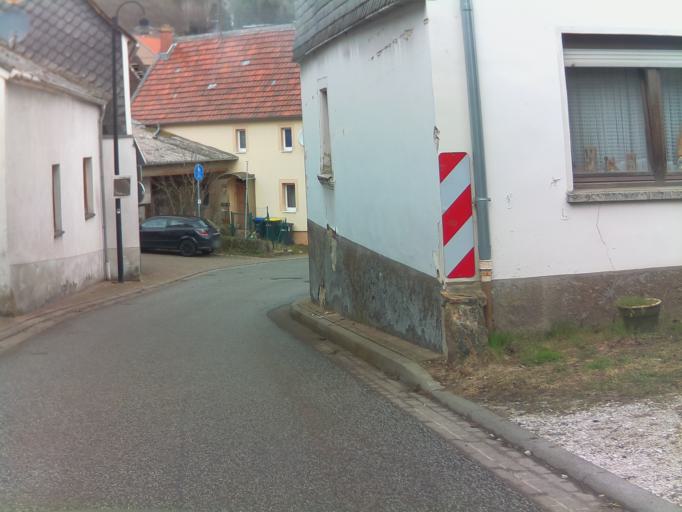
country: DE
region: Rheinland-Pfalz
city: Seibersbach
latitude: 49.9596
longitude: 7.7153
